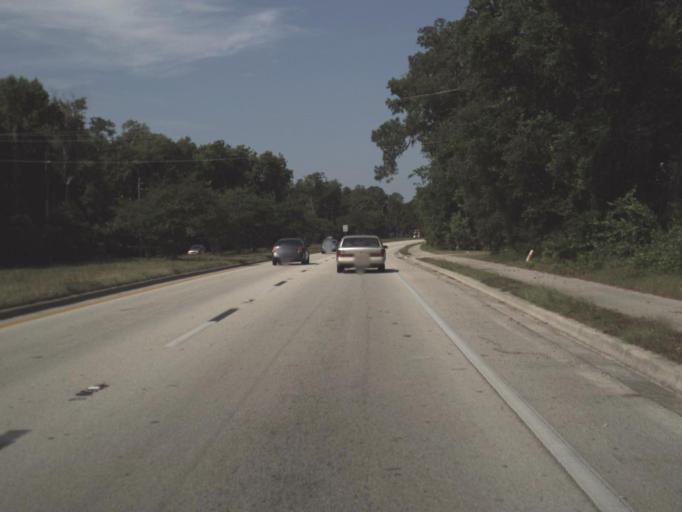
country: US
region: Florida
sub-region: Saint Johns County
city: Saint Augustine South
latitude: 29.8633
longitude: -81.3447
